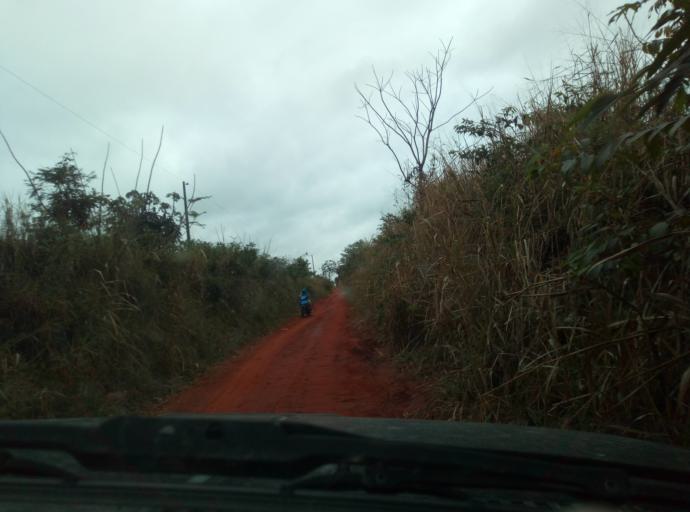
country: PY
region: Caaguazu
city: Doctor Cecilio Baez
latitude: -25.1584
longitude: -56.2716
